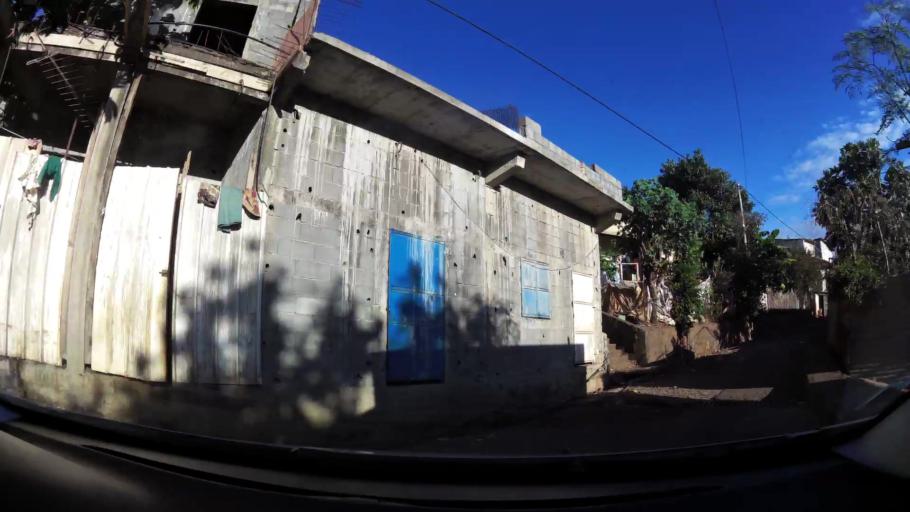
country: YT
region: Koungou
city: Koungou
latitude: -12.7332
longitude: 45.2061
